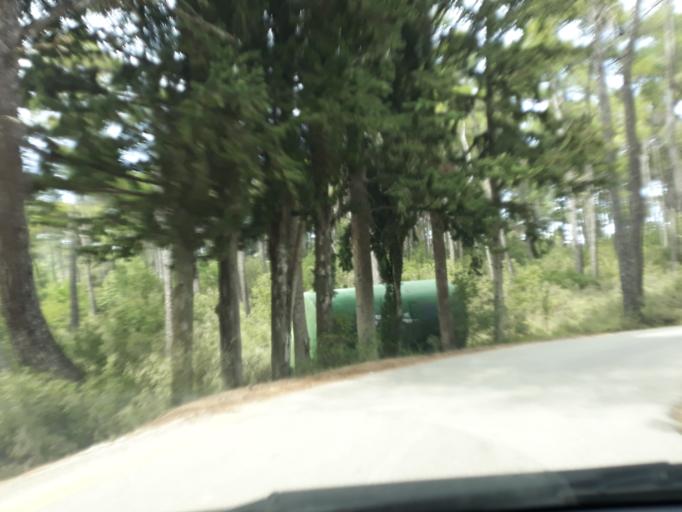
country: GR
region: Attica
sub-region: Nomarchia Anatolikis Attikis
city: Varybobi
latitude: 38.1609
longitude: 23.7875
